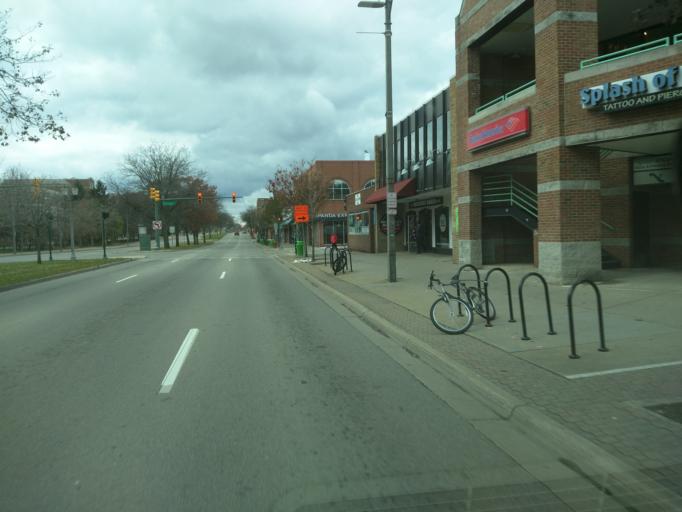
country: US
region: Michigan
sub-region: Ingham County
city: East Lansing
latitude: 42.7337
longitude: -84.4779
